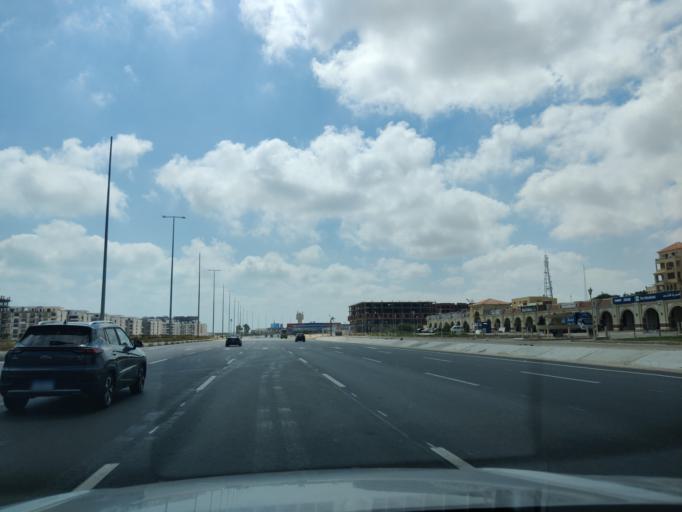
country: EG
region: Muhafazat Matruh
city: Al `Alamayn
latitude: 30.8455
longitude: 28.9358
